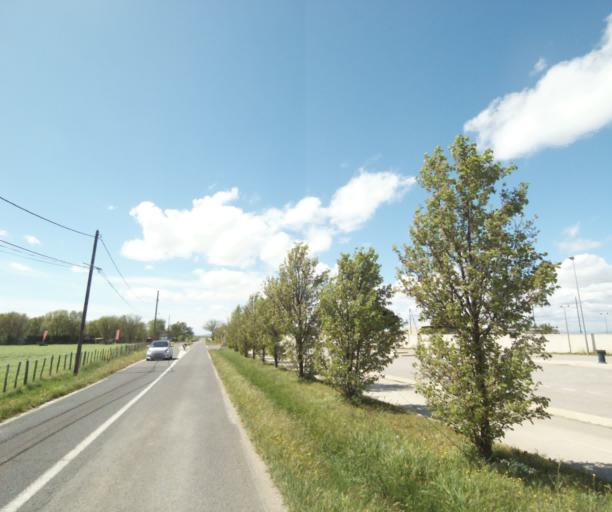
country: FR
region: Languedoc-Roussillon
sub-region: Departement de l'Herault
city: Perols
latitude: 43.5595
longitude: 3.9371
